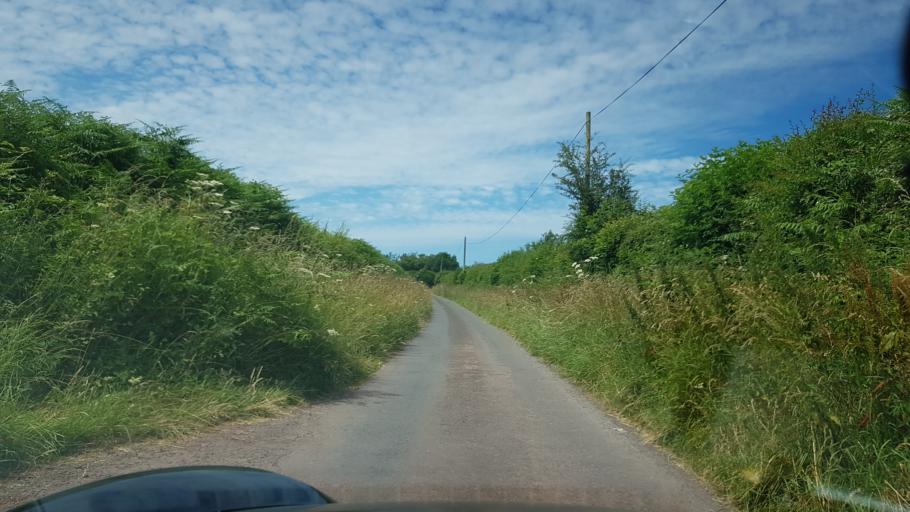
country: GB
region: Wales
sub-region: Carmarthenshire
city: Saint Clears
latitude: 51.7709
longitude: -4.4776
